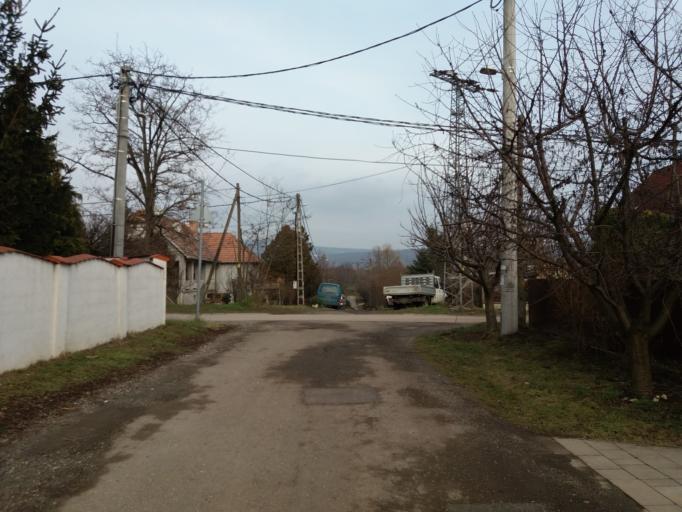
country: HU
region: Pest
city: Paty
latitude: 47.5155
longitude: 18.8132
